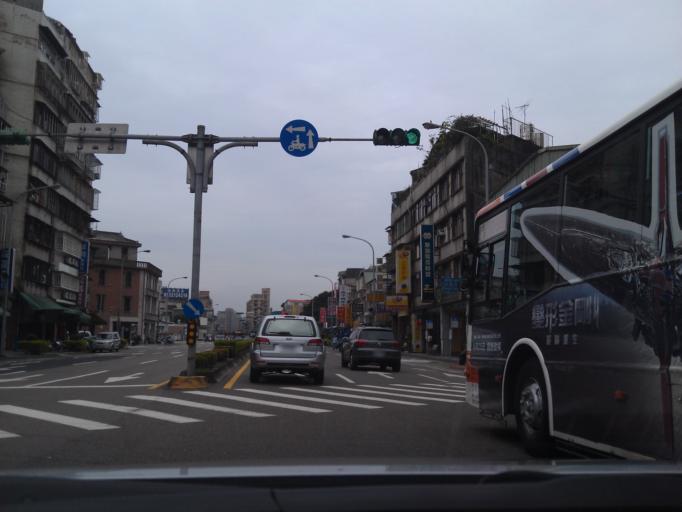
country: TW
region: Taipei
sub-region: Taipei
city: Banqiao
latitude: 25.0335
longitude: 121.4981
